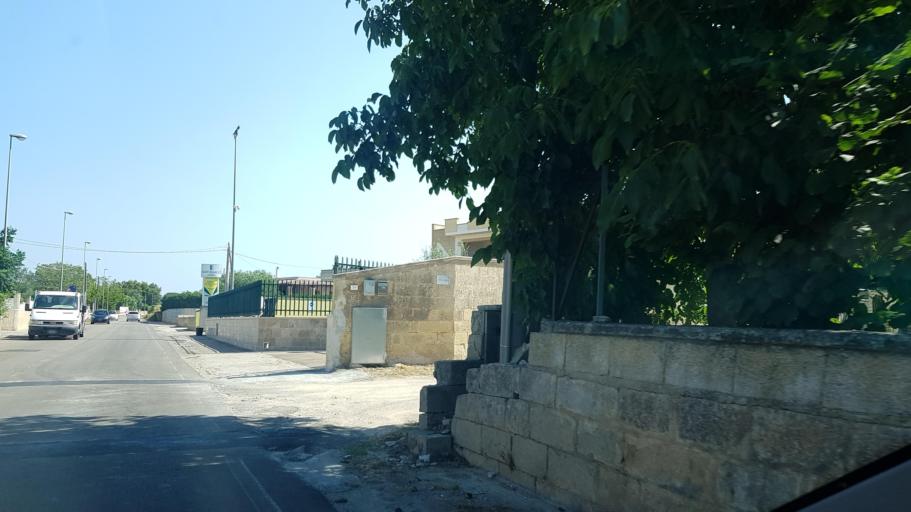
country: IT
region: Apulia
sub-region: Provincia di Lecce
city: Ruffano
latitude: 39.9901
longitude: 18.2615
